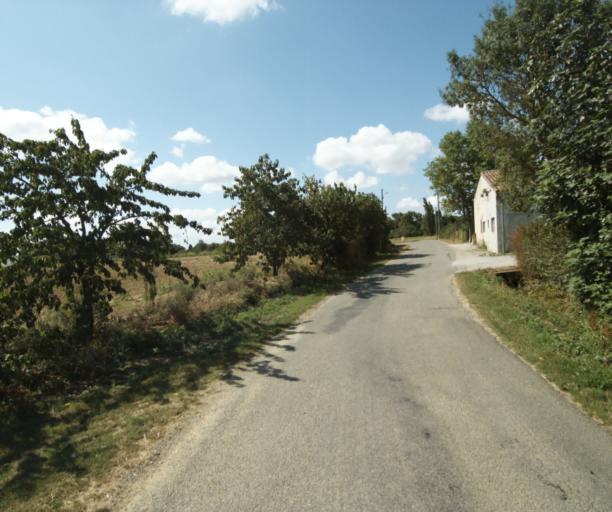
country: FR
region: Midi-Pyrenees
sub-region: Departement de la Haute-Garonne
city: Auriac-sur-Vendinelle
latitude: 43.4519
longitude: 1.7897
